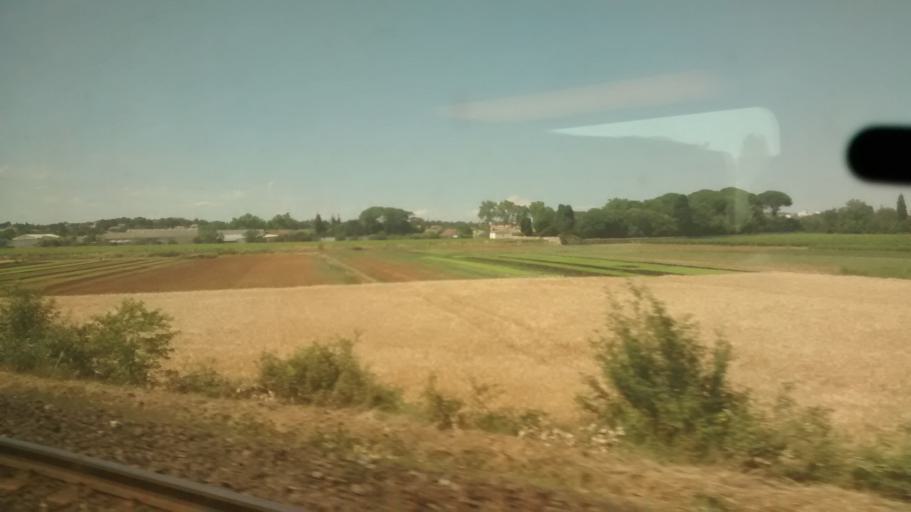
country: FR
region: Languedoc-Roussillon
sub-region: Departement de l'Herault
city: Le Cres
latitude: 43.6386
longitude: 3.9496
